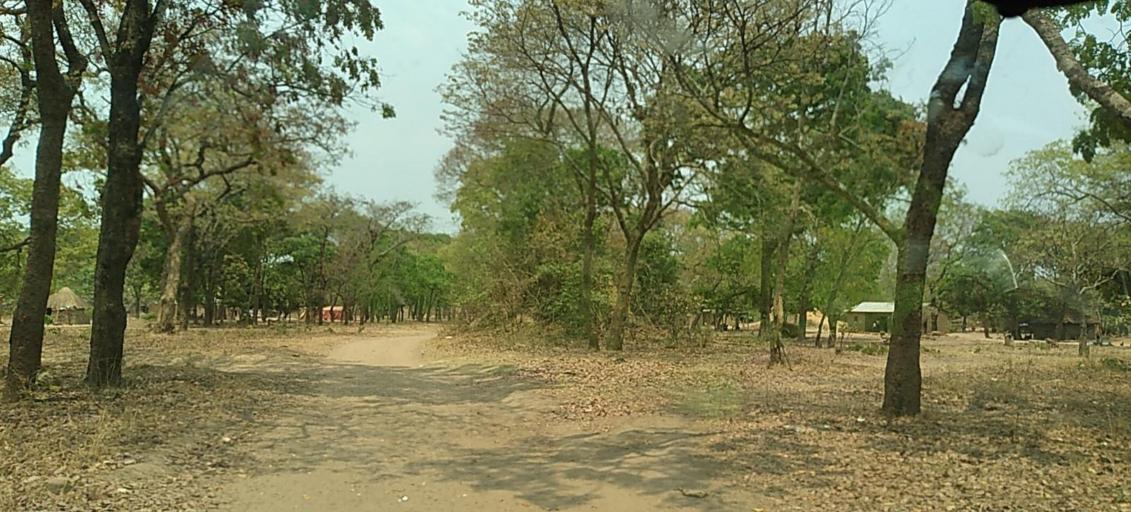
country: ZM
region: North-Western
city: Kabompo
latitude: -13.5678
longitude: 24.4421
